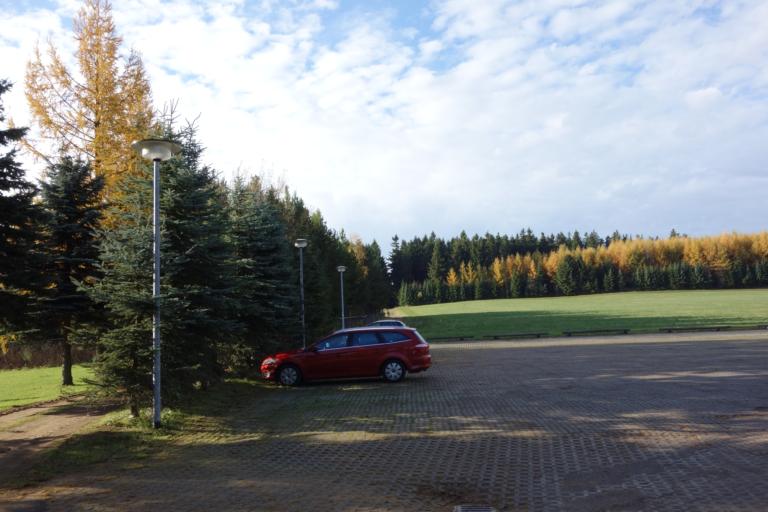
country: DE
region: Saxony
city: Neuhausen
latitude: 50.7113
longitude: 13.4663
